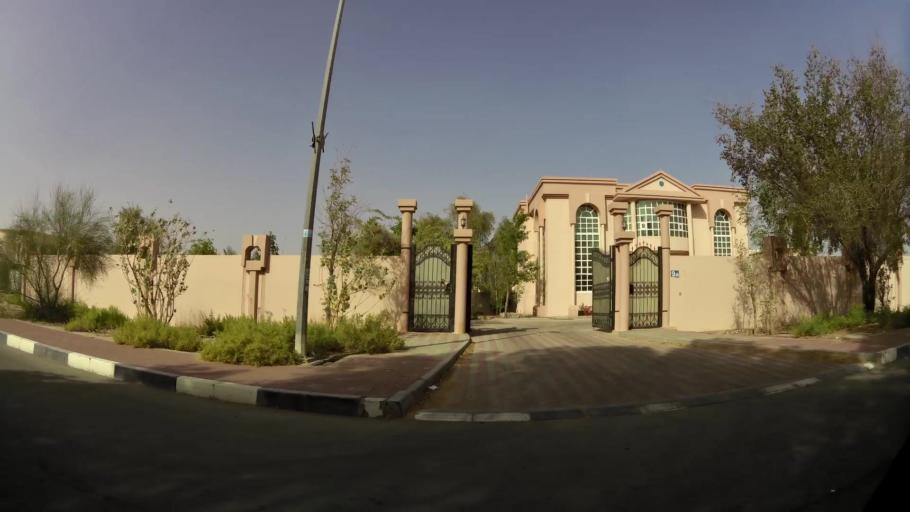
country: AE
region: Abu Dhabi
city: Al Ain
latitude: 24.2367
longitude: 55.6700
